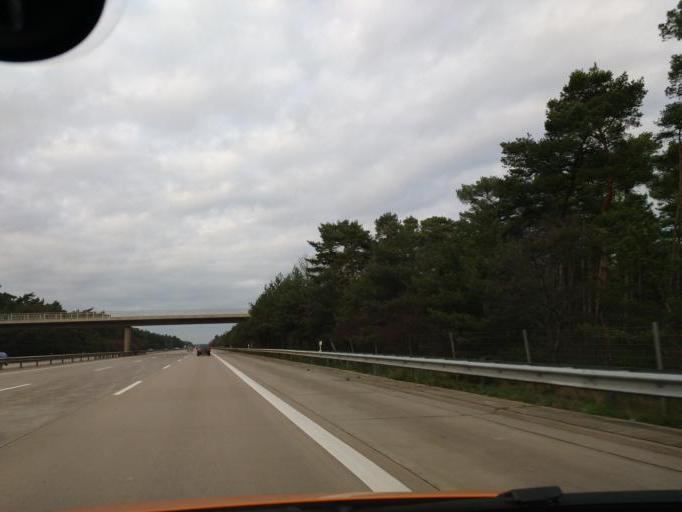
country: DE
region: Lower Saxony
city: Lindwedel
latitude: 52.6285
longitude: 9.7237
